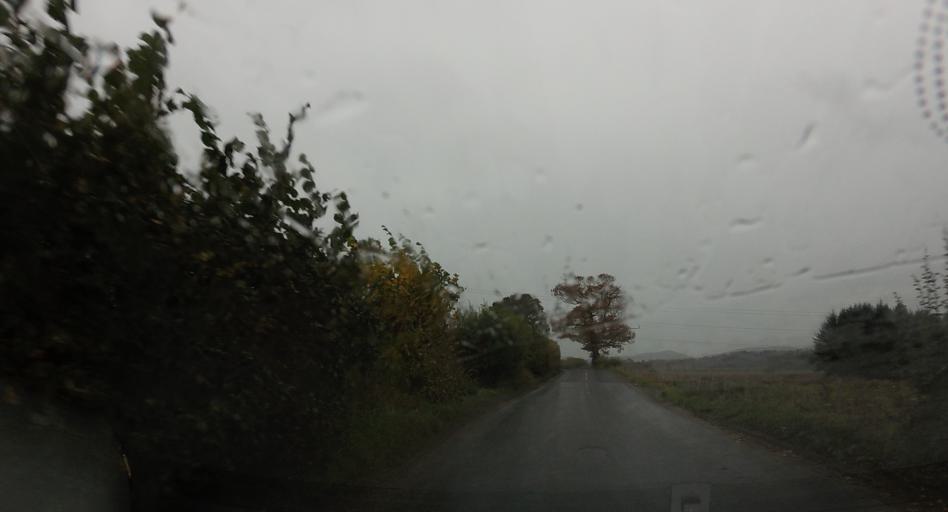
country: GB
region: Scotland
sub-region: Perth and Kinross
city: Blairgowrie
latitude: 56.5497
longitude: -3.3205
